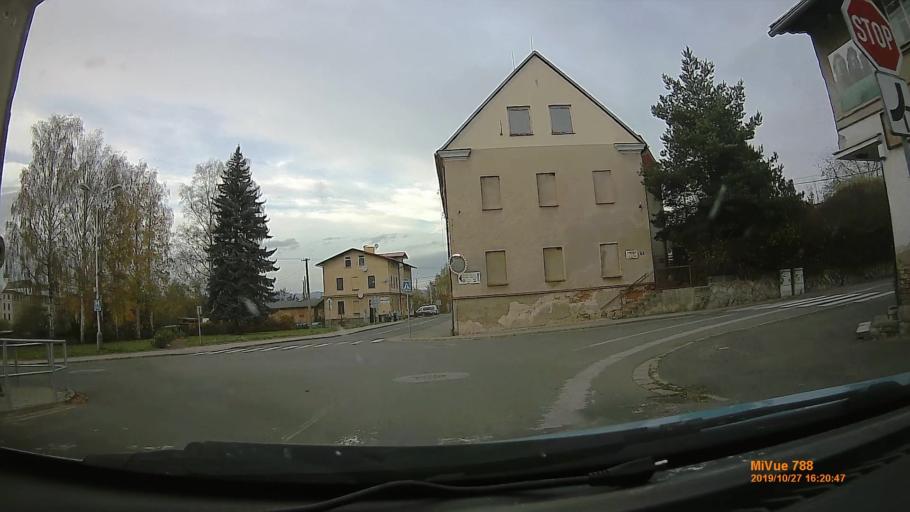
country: CZ
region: Kralovehradecky
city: Broumov
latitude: 50.5821
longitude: 16.3410
